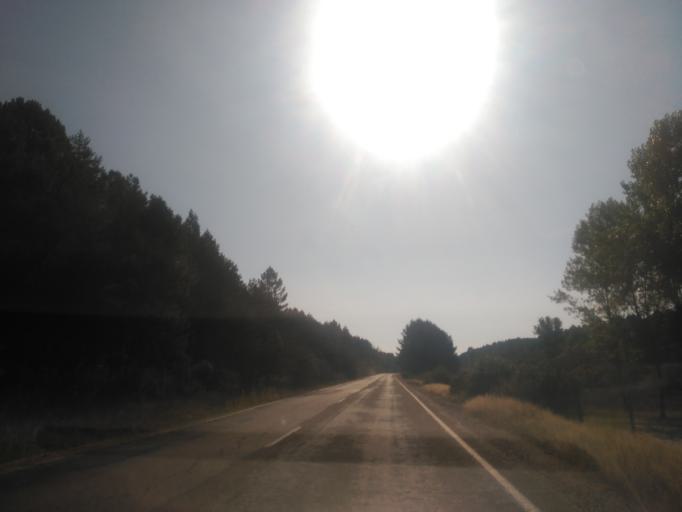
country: ES
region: Castille and Leon
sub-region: Provincia de Soria
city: San Leonardo de Yague
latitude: 41.8115
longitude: -3.0608
